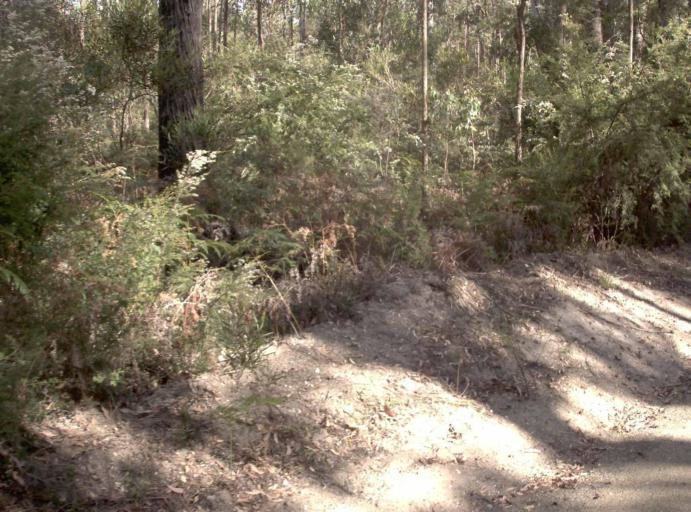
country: AU
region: Victoria
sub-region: East Gippsland
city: Lakes Entrance
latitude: -37.6799
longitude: 148.0538
